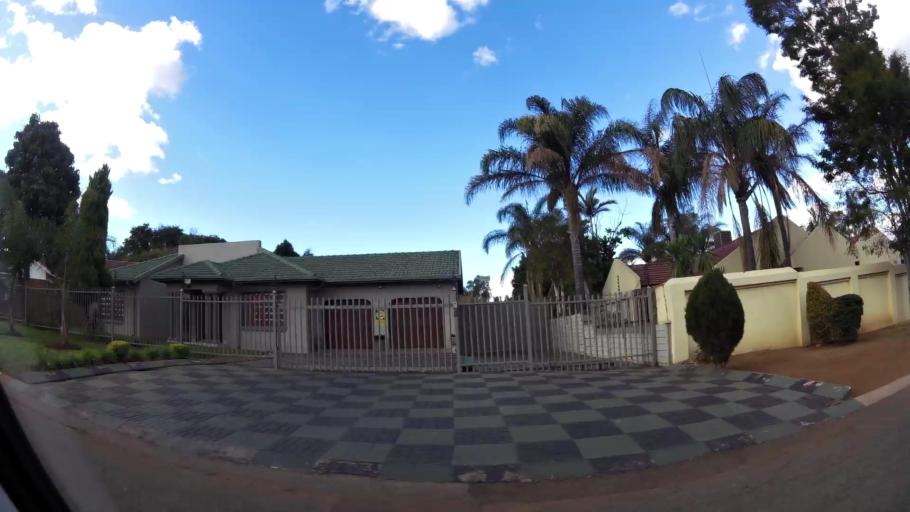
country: ZA
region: Limpopo
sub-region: Capricorn District Municipality
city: Polokwane
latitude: -23.9019
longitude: 29.4970
